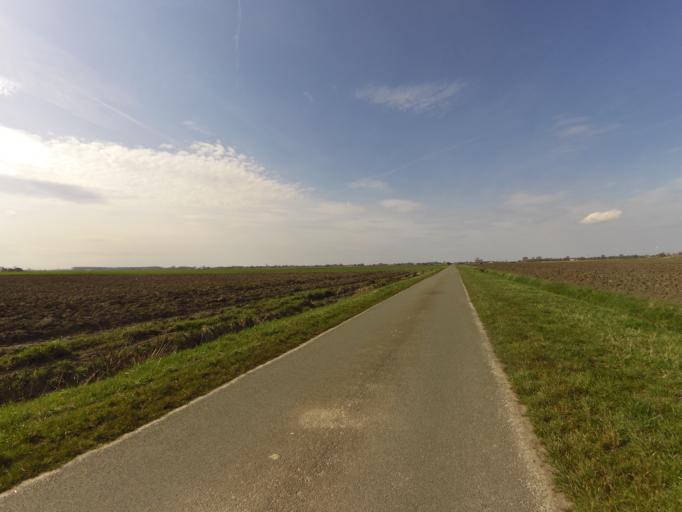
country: BE
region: Flanders
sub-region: Provincie West-Vlaanderen
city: Gistel
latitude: 51.1267
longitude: 2.9508
